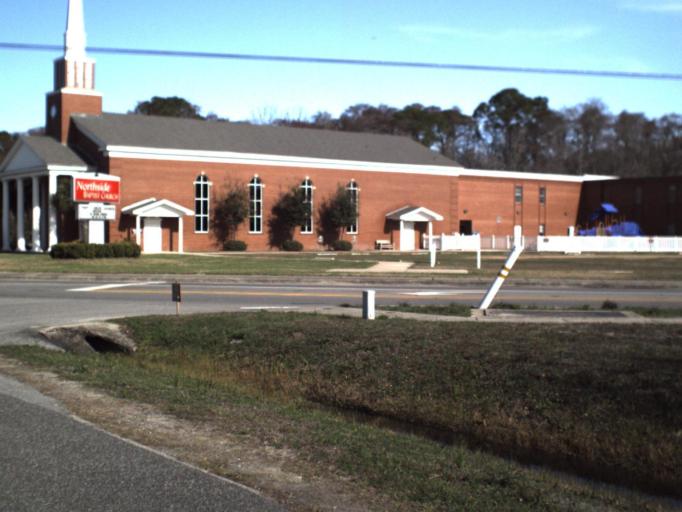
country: US
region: Florida
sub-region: Bay County
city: Panama City
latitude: 30.1822
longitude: -85.6674
